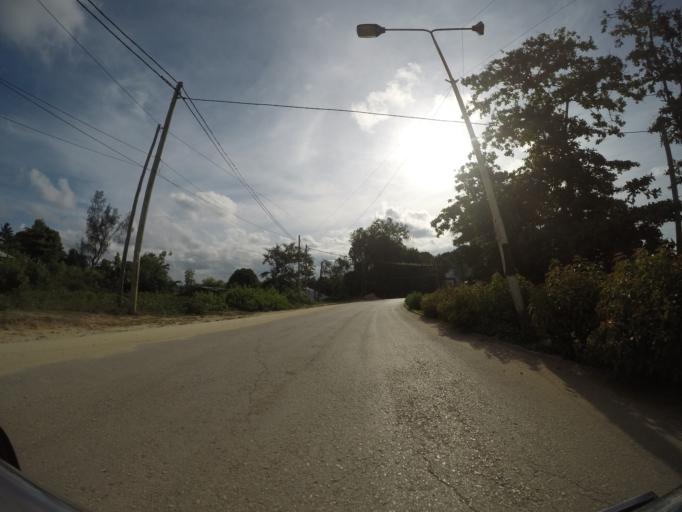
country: TZ
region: Pemba South
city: Chake Chake
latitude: -5.2363
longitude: 39.7770
